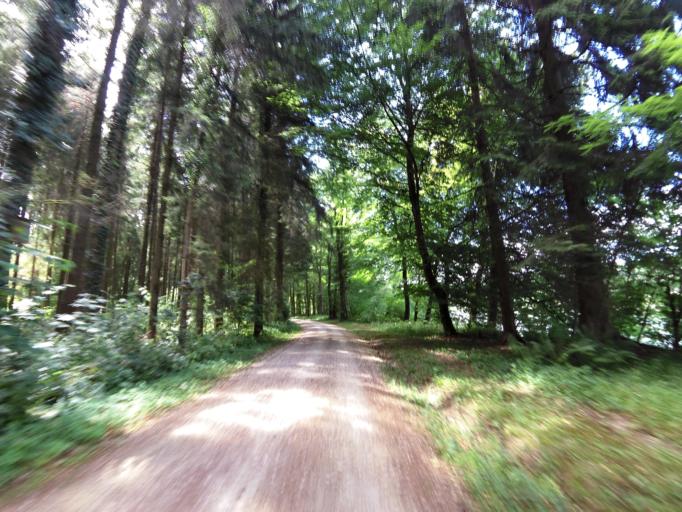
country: DE
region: Baden-Wuerttemberg
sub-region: Freiburg Region
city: Schworstadt
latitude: 47.5807
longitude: 7.9009
